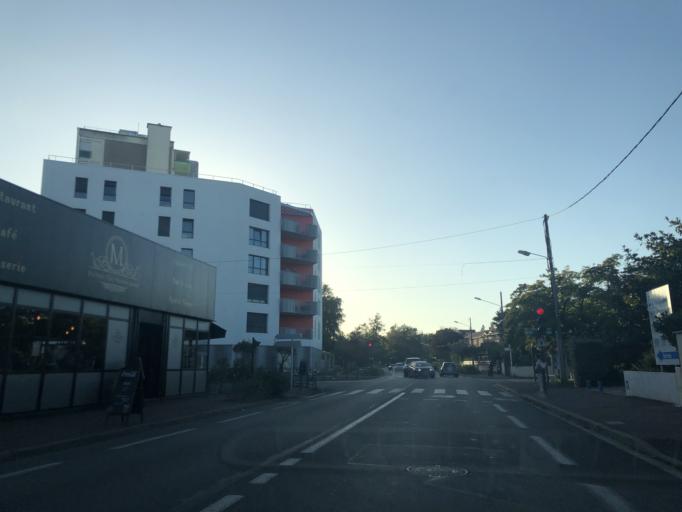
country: FR
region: Aquitaine
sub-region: Departement de la Gironde
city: Merignac
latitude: 44.8464
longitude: -0.6334
